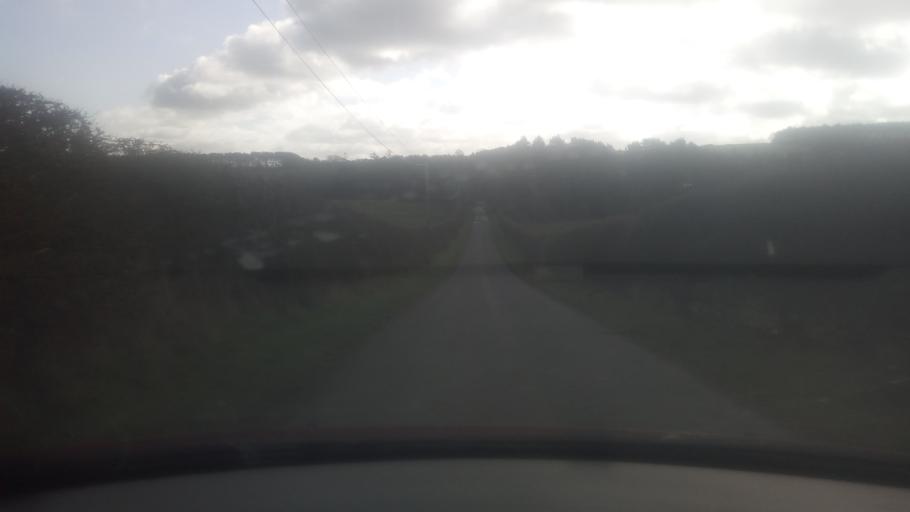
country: GB
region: Scotland
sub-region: The Scottish Borders
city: Saint Boswells
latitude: 55.5222
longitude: -2.6547
